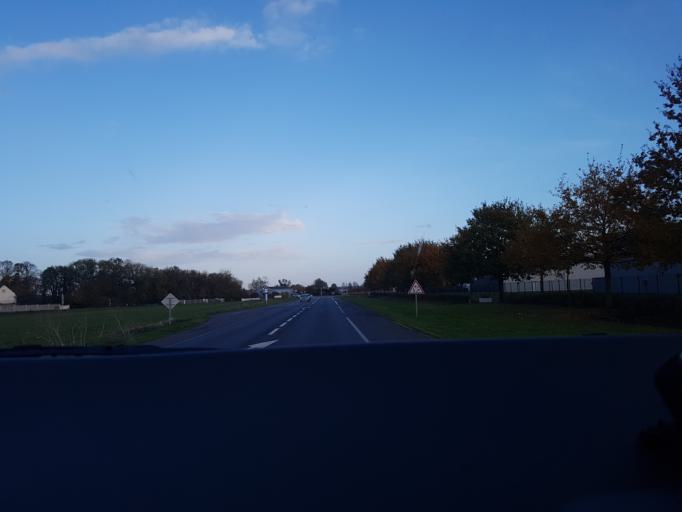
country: FR
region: Lower Normandy
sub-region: Departement du Calvados
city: Demouville
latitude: 49.1731
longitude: -0.2684
